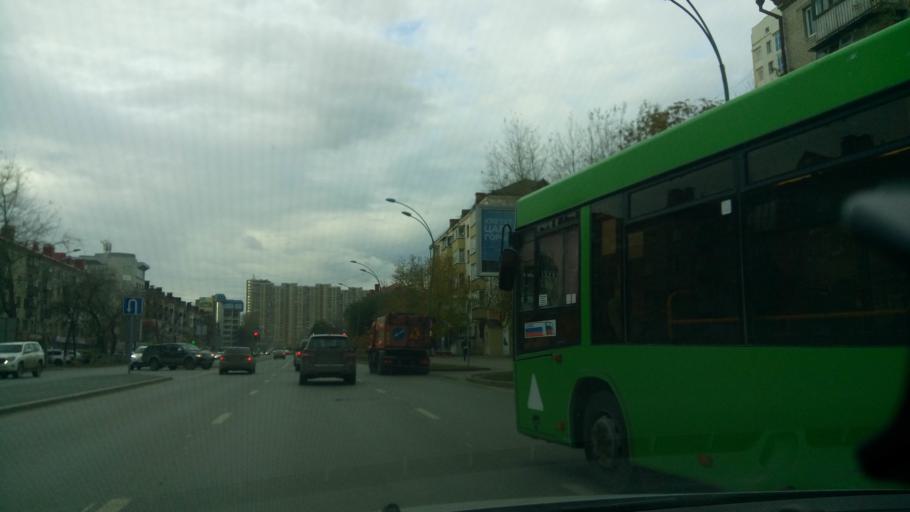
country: RU
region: Tjumen
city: Tyumen
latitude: 57.1406
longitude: 65.5736
